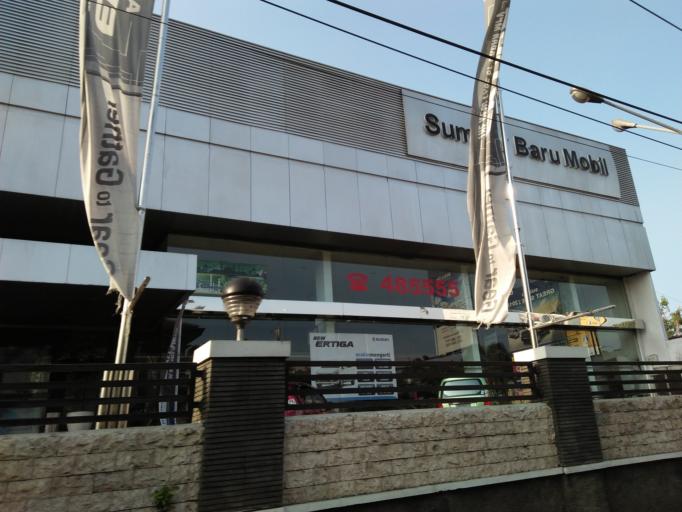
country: ID
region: Daerah Istimewa Yogyakarta
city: Depok
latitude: -7.7832
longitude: 110.4174
